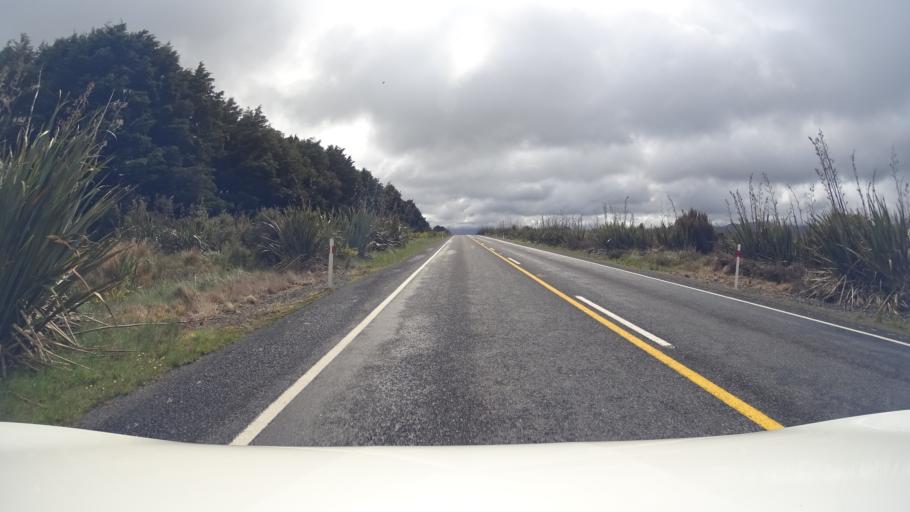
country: NZ
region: Manawatu-Wanganui
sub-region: Ruapehu District
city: Waiouru
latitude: -39.1800
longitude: 175.4503
